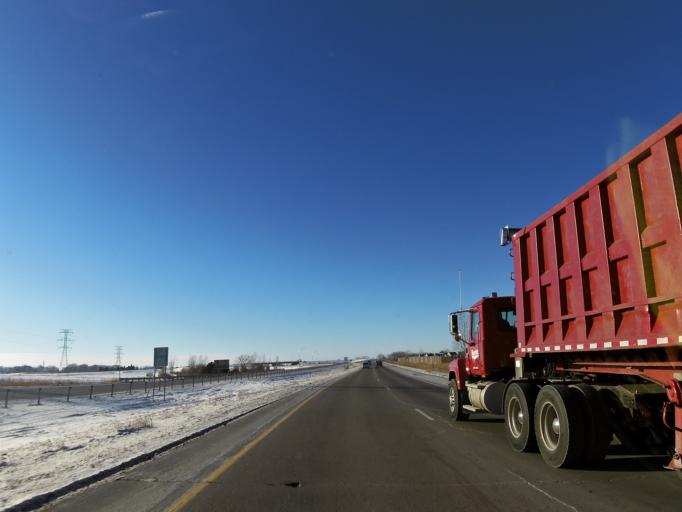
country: US
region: Minnesota
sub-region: Scott County
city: Shakopee
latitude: 44.7766
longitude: -93.5489
